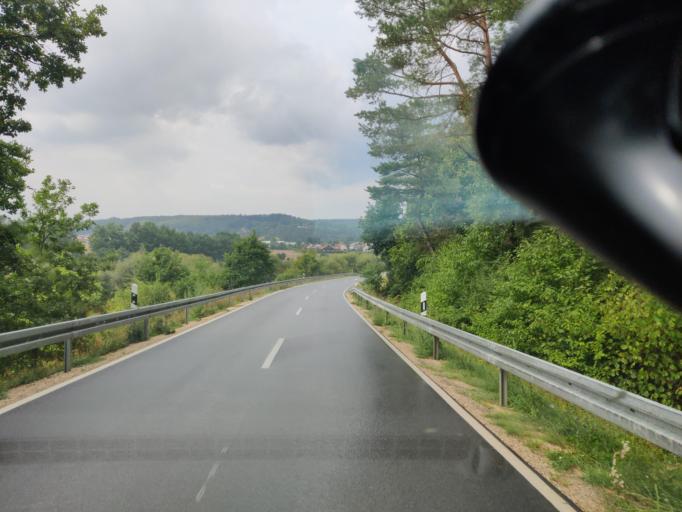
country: DE
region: Bavaria
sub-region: Regierungsbezirk Mittelfranken
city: Heideck
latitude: 49.1254
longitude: 11.1249
